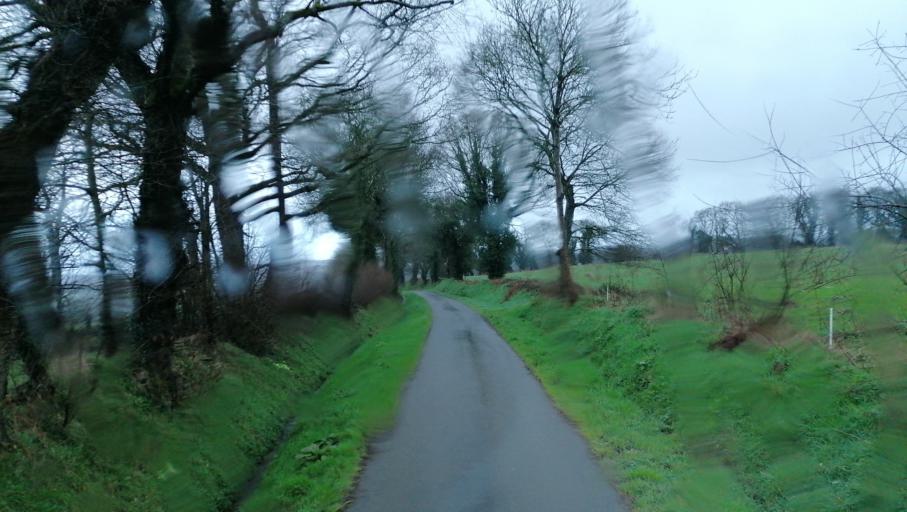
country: FR
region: Brittany
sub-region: Departement des Cotes-d'Armor
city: Lanrodec
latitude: 48.4794
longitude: -2.9870
